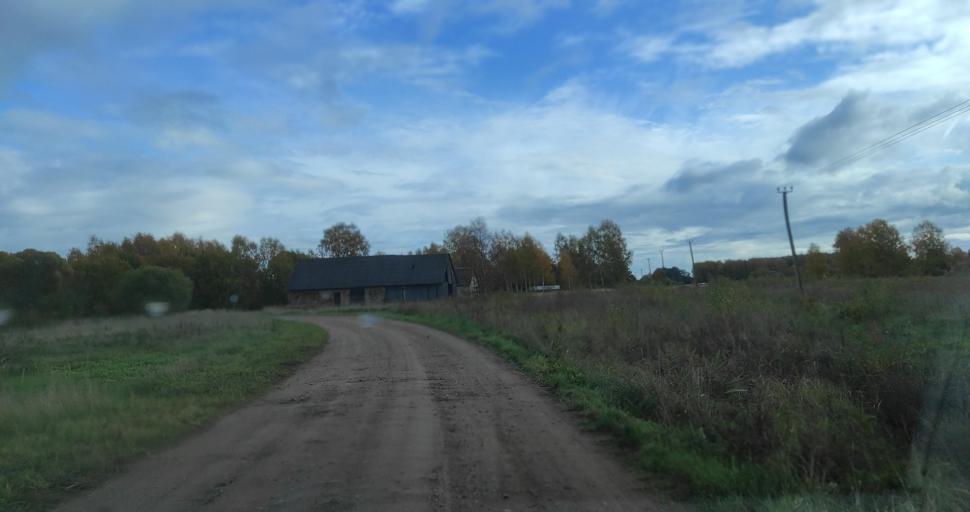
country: LV
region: Skrunda
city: Skrunda
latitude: 56.6852
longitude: 21.9943
